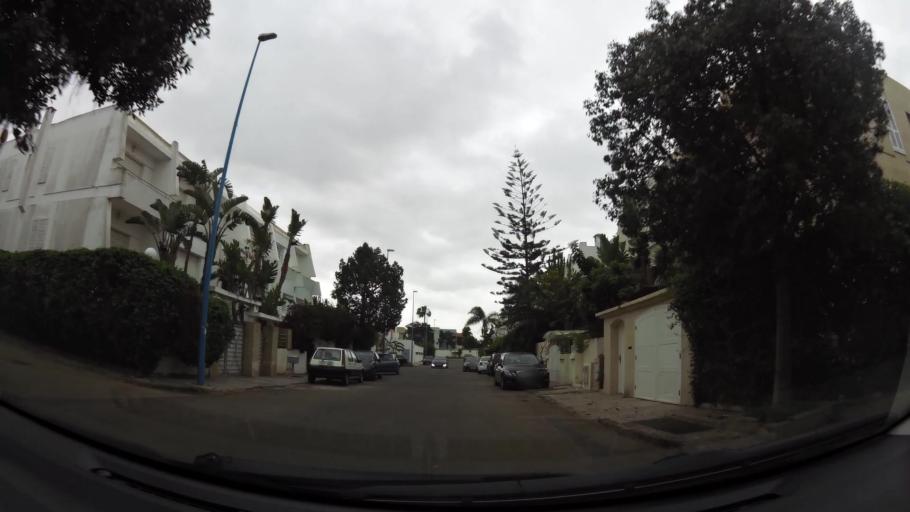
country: MA
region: Grand Casablanca
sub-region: Casablanca
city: Casablanca
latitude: 33.5961
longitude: -7.6569
